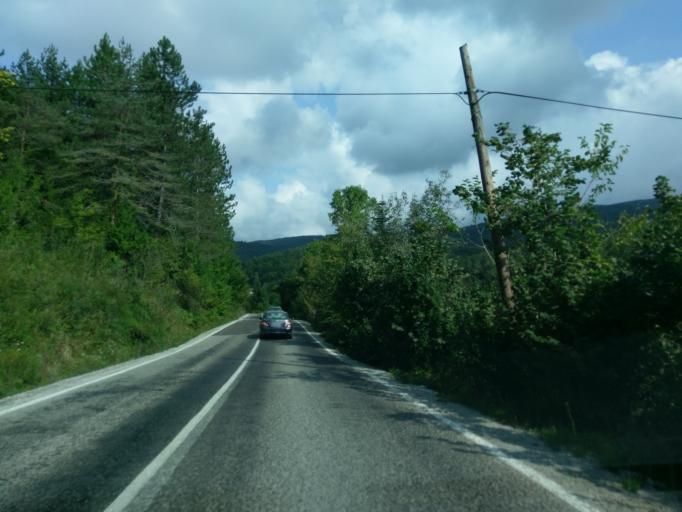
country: TR
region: Sinop
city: Ayancik
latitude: 41.8820
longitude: 34.5202
